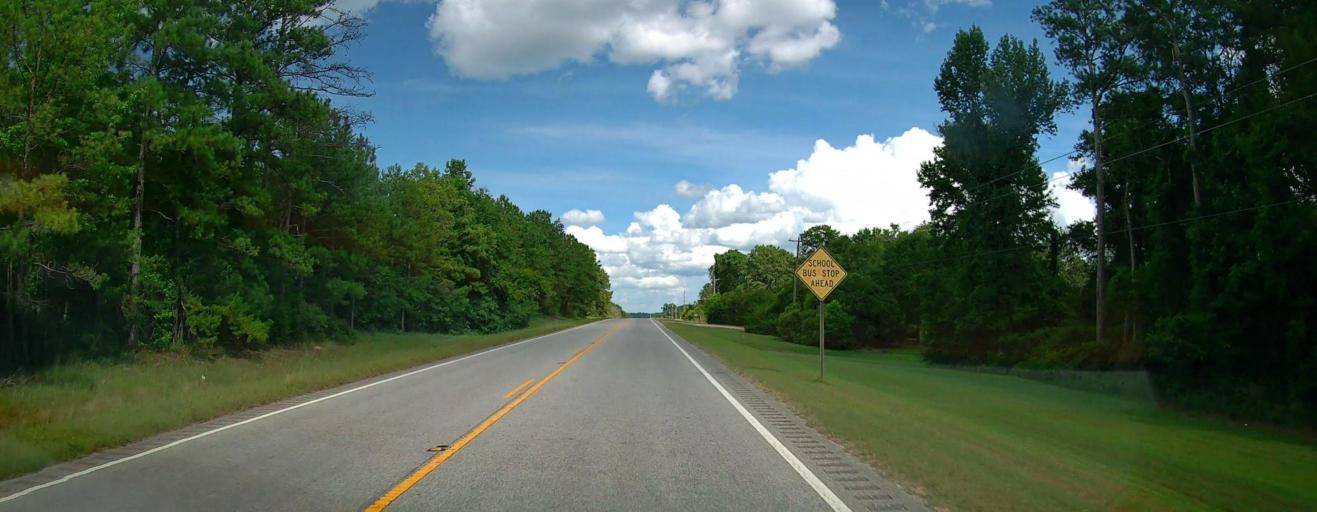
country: US
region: Alabama
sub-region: Macon County
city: Tuskegee
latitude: 32.4602
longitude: -85.5537
